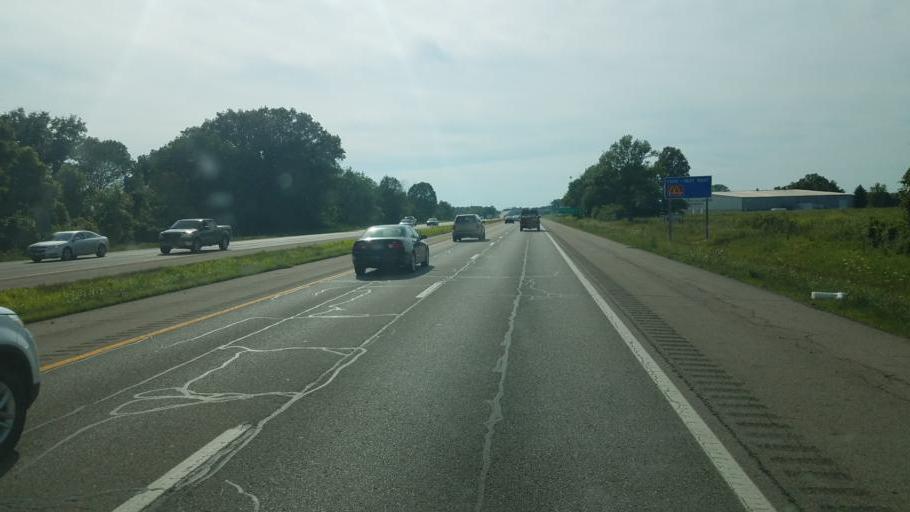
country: US
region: Ohio
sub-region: Fairfield County
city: Canal Winchester
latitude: 39.8404
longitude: -82.7679
